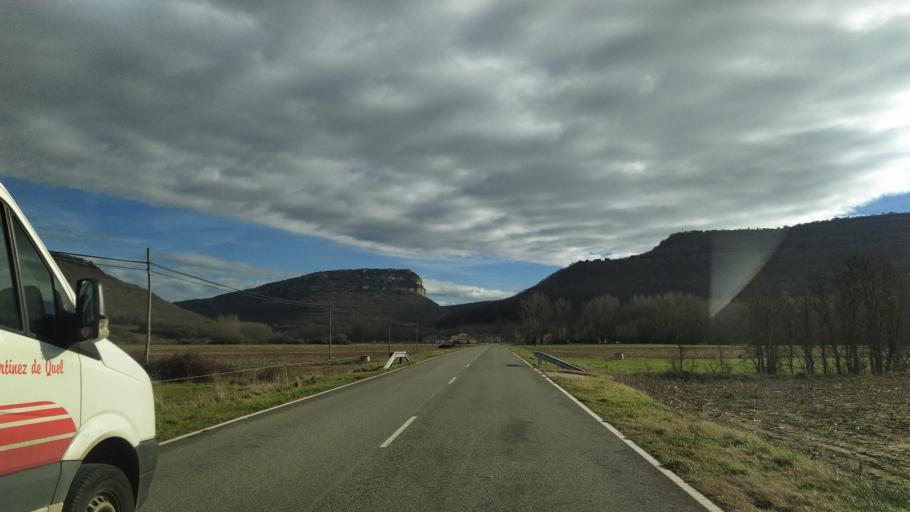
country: ES
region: Cantabria
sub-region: Provincia de Cantabria
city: San Martin de Elines
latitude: 42.8348
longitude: -3.8682
